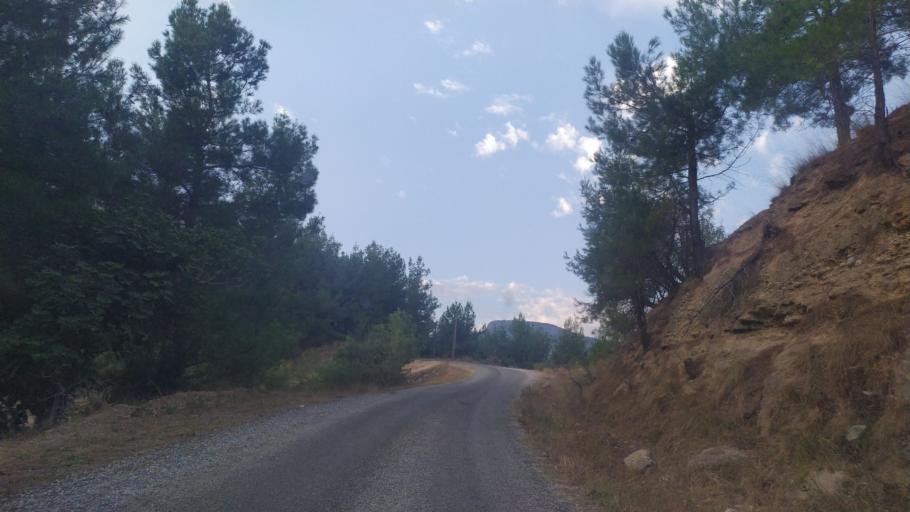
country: TR
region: Mersin
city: Camliyayla
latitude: 37.2246
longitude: 34.7108
